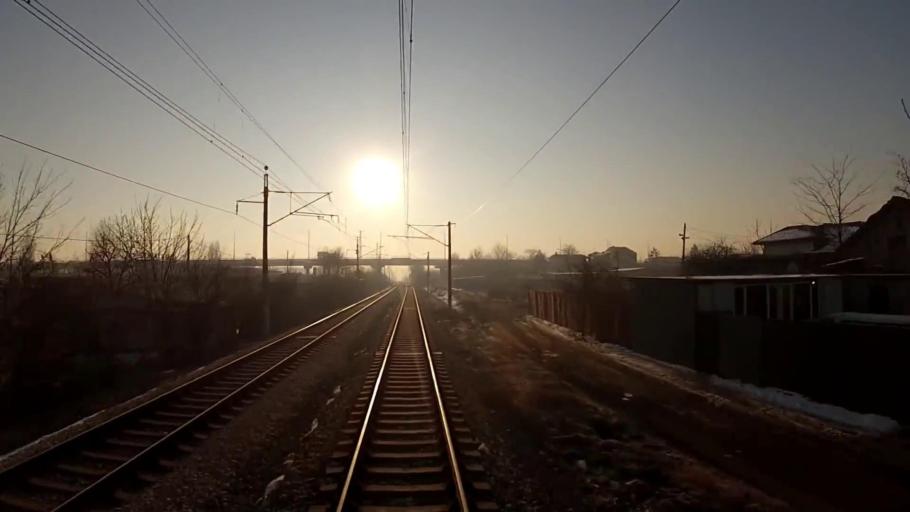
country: BG
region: Sofiya
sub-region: Obshtina Bozhurishte
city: Bozhurishte
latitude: 42.7363
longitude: 23.2662
